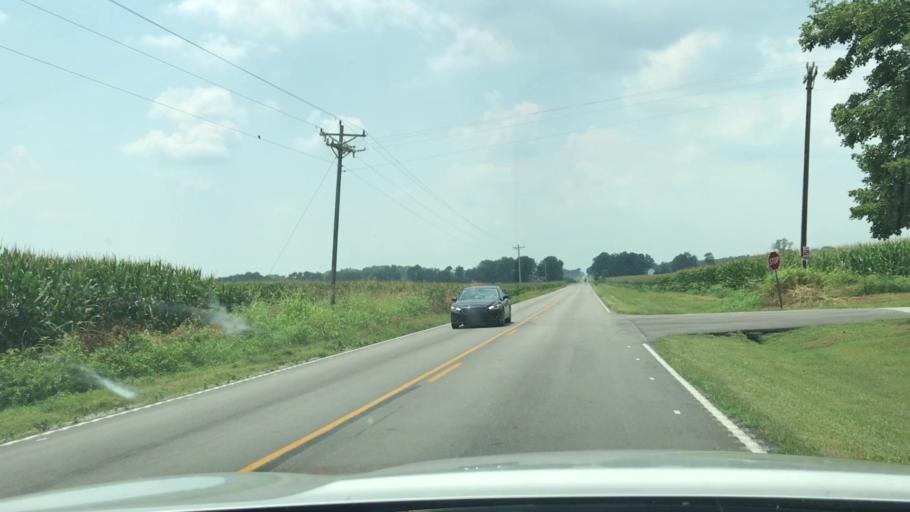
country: US
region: Kentucky
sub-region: Todd County
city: Guthrie
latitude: 36.6995
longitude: -87.1180
